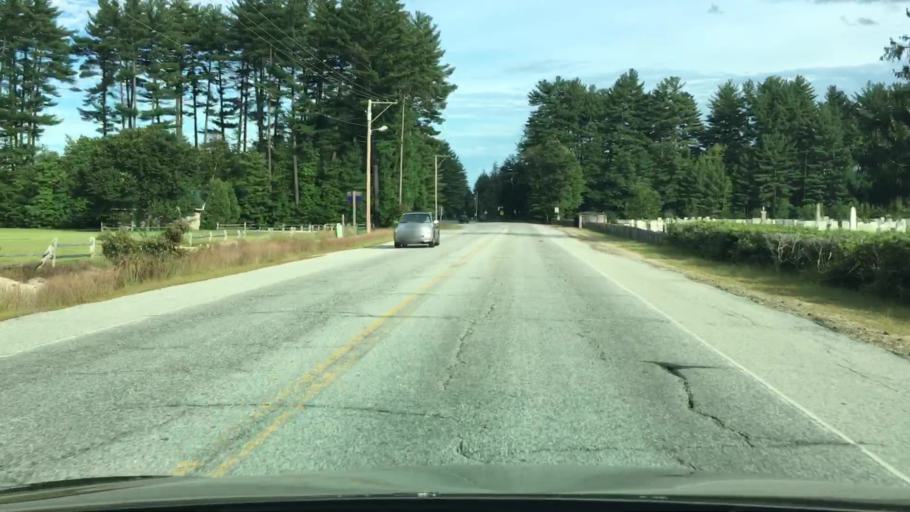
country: US
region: Maine
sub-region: Oxford County
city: Fryeburg
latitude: 44.0209
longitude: -70.9722
